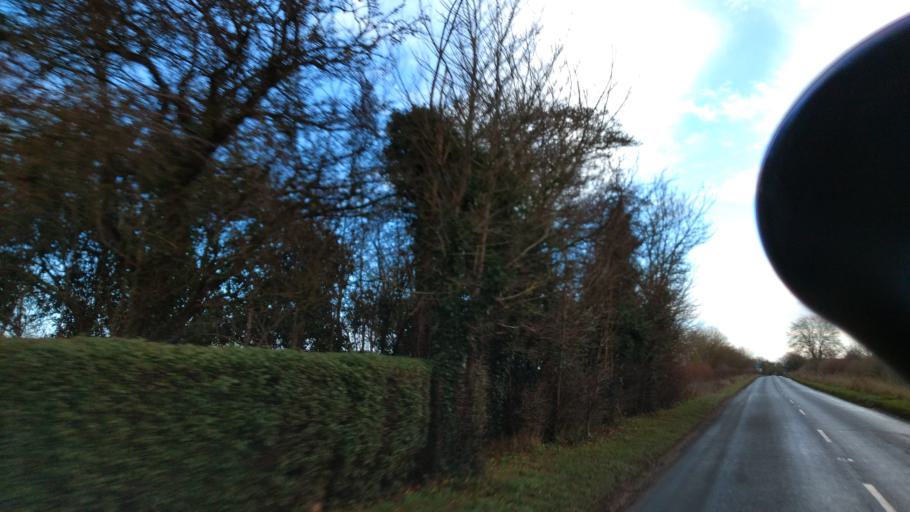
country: GB
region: England
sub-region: Borough of Swindon
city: Highworth
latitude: 51.6193
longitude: -1.6958
